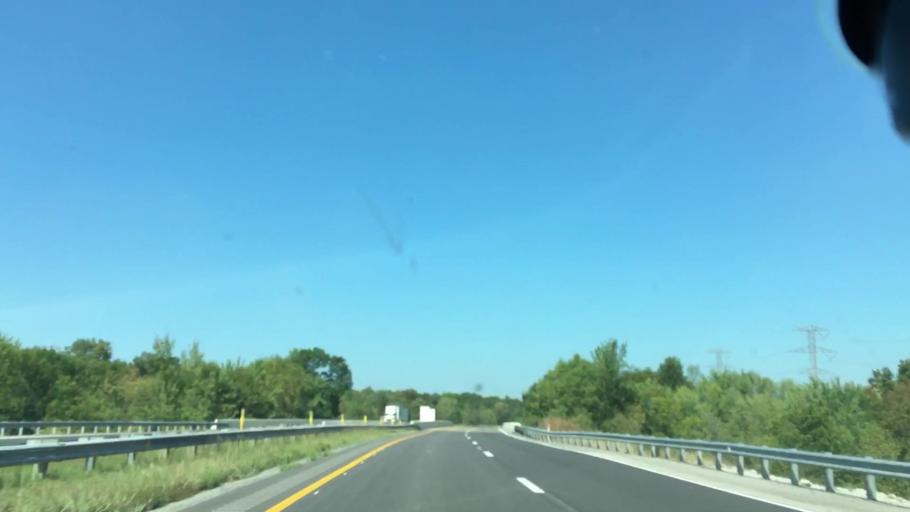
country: US
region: Kentucky
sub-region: Webster County
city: Sebree
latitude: 37.6253
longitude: -87.5075
